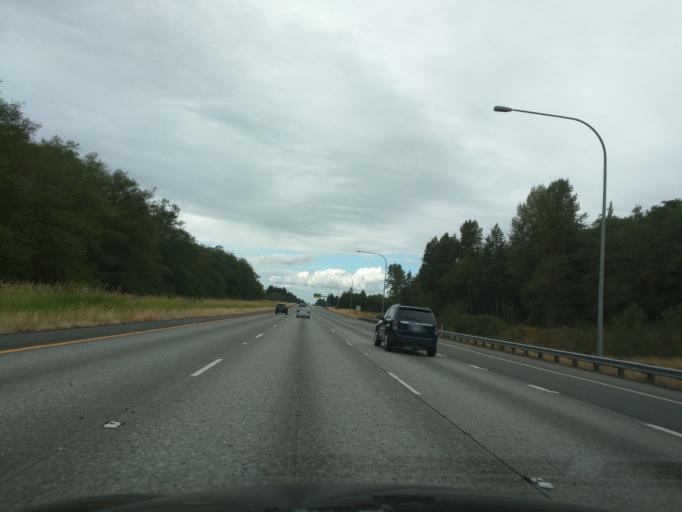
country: US
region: Washington
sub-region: Snohomish County
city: Bryant
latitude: 48.2628
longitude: -122.2626
